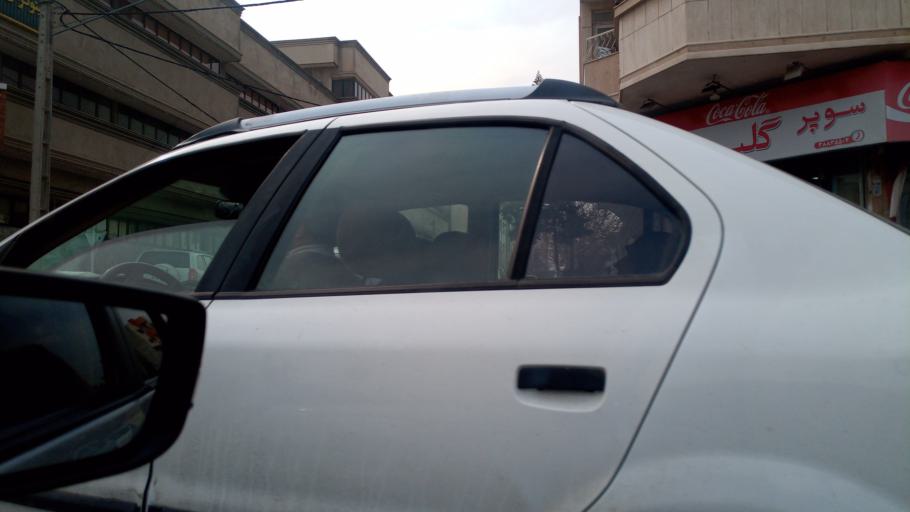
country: IR
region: Razavi Khorasan
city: Mashhad
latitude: 36.3116
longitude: 59.5110
